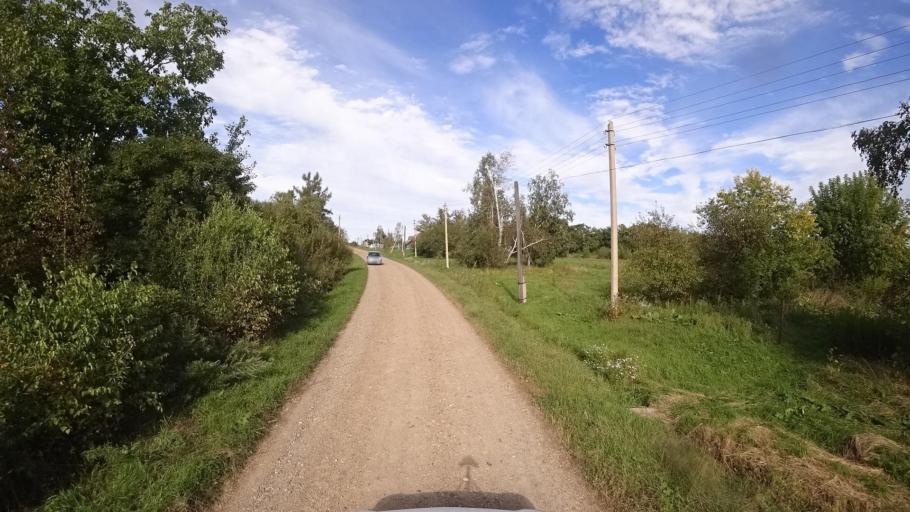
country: RU
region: Primorskiy
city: Dostoyevka
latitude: 44.2965
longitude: 133.4493
